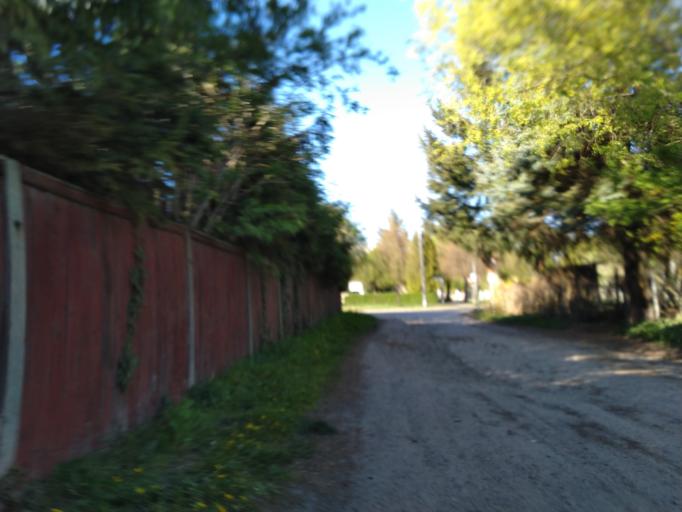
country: DE
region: Brandenburg
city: Wriezen
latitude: 52.7141
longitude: 14.1386
